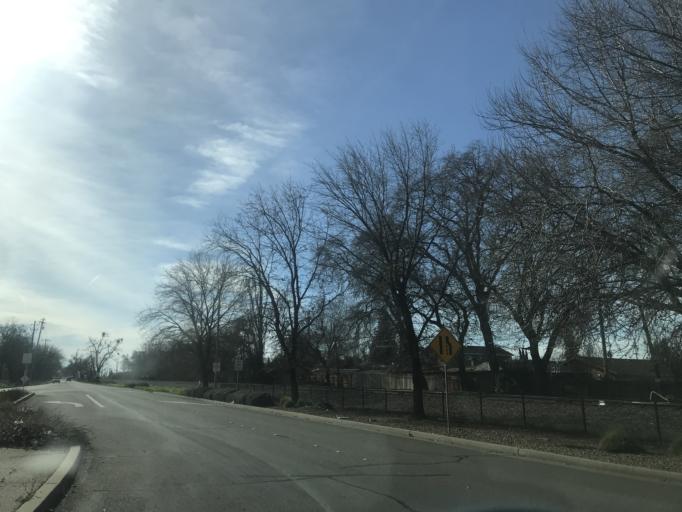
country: US
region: California
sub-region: Yolo County
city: Woodland
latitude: 38.6599
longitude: -121.7657
